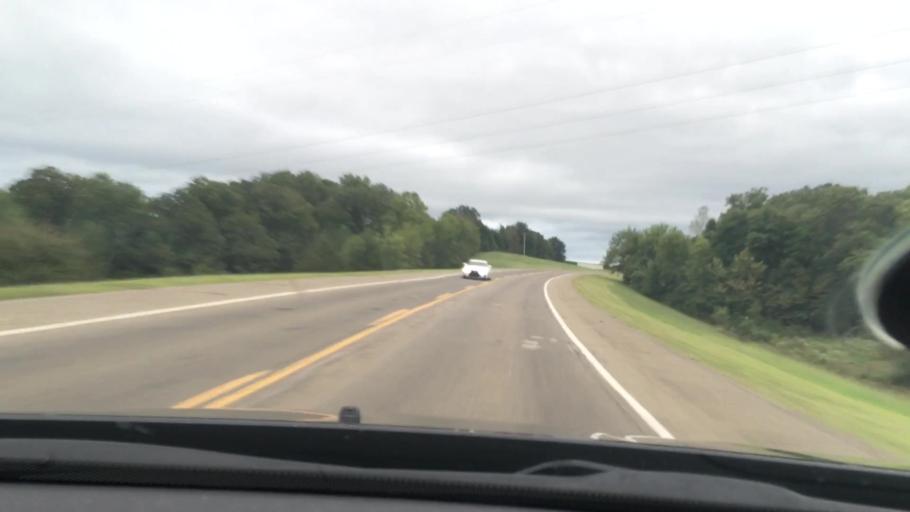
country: US
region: Oklahoma
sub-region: Sequoyah County
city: Vian
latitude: 35.5158
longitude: -94.9713
